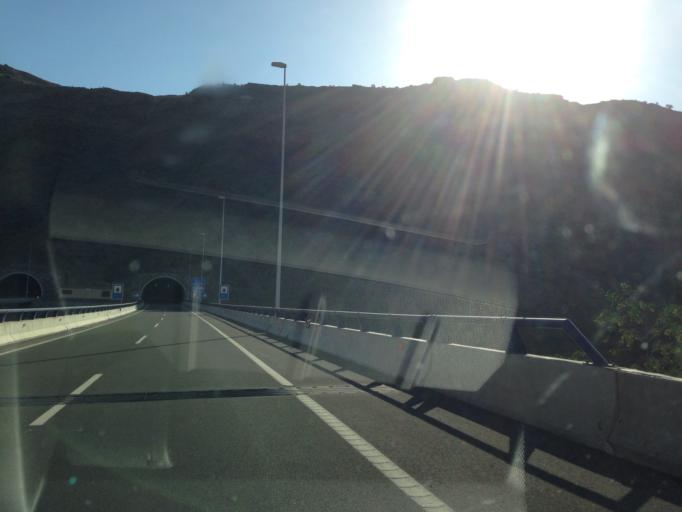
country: ES
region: Canary Islands
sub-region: Provincia de Las Palmas
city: Puerto Rico
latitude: 27.8094
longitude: -15.7254
